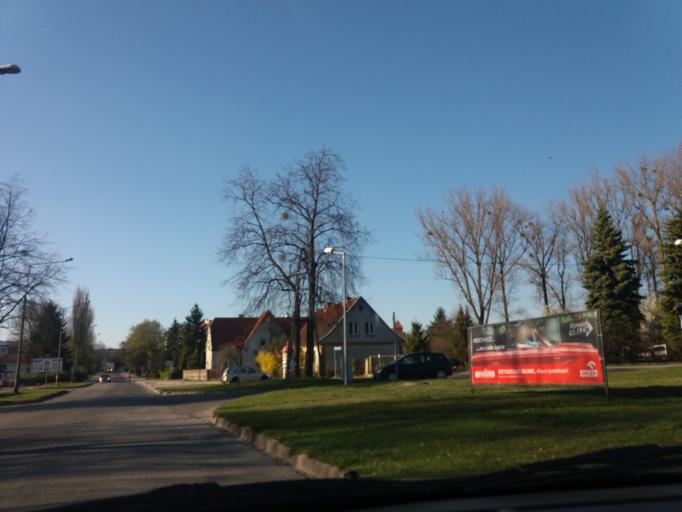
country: PL
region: Warmian-Masurian Voivodeship
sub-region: Powiat nidzicki
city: Nidzica
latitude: 53.3530
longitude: 20.4279
